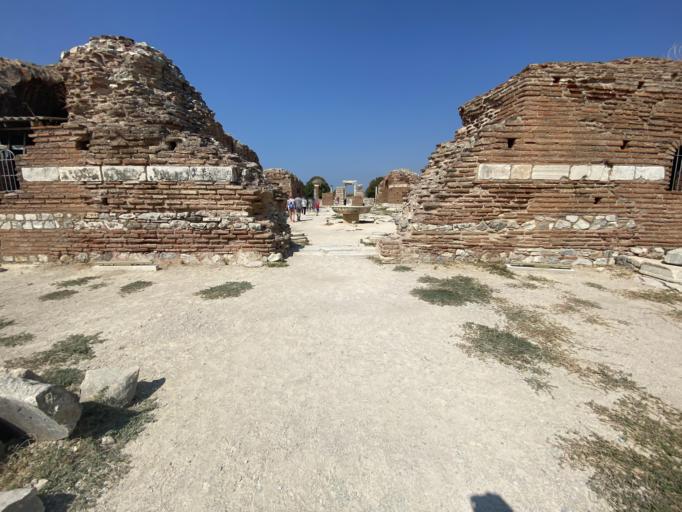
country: TR
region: Izmir
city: Selcuk
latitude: 37.9450
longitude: 27.3396
